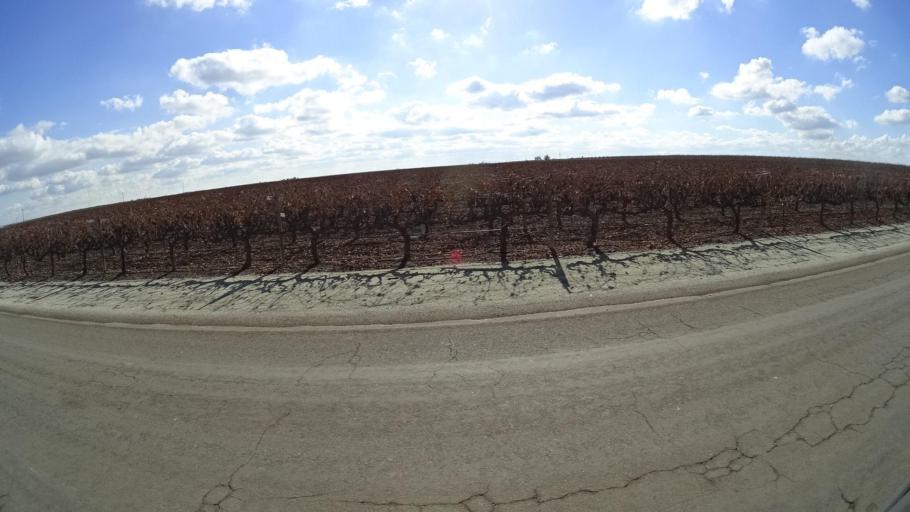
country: US
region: California
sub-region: Kern County
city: Delano
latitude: 35.7323
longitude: -119.2746
